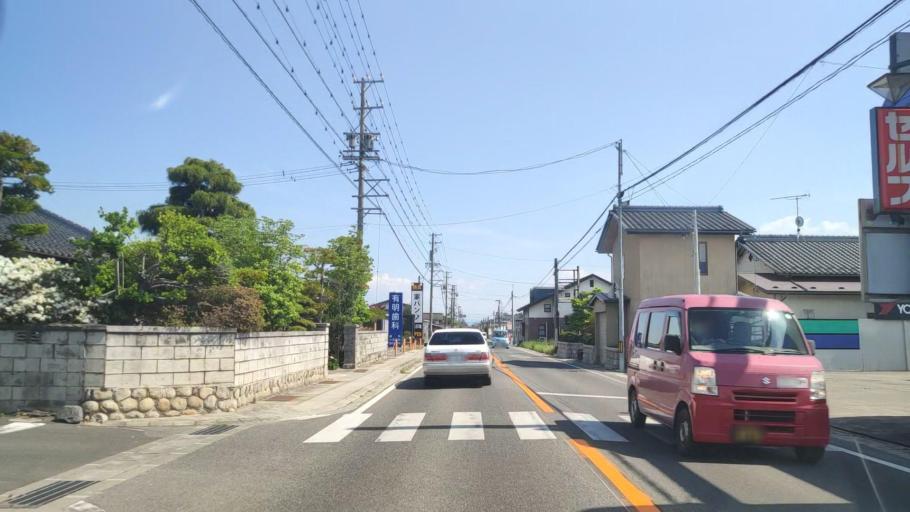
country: JP
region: Nagano
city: Hotaka
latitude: 36.3622
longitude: 137.8780
